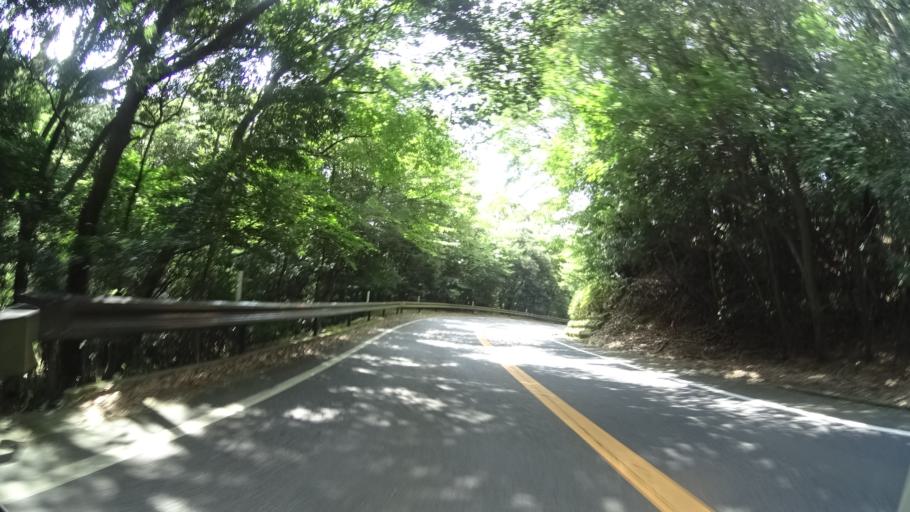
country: JP
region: Miyazaki
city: Kobayashi
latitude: 31.8974
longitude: 130.8358
